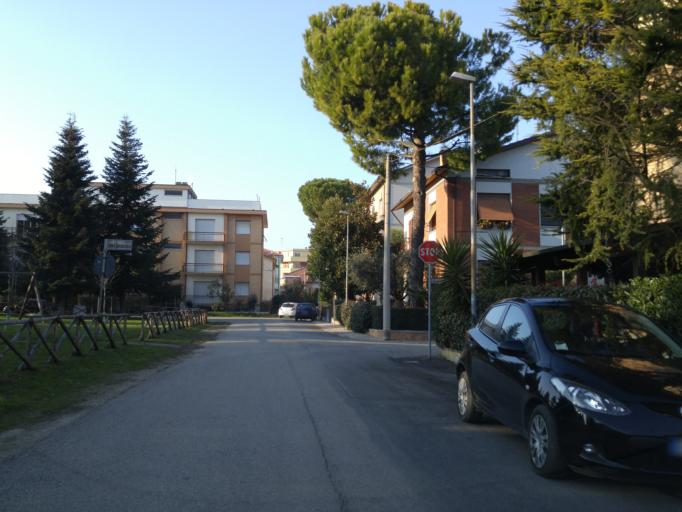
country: IT
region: The Marches
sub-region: Provincia di Pesaro e Urbino
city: Fano
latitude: 43.8343
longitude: 13.0070
